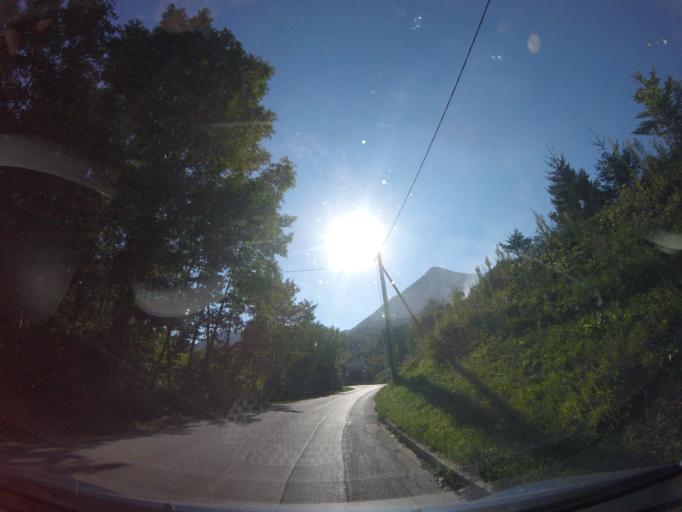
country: HR
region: Zagrebacka
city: Rude
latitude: 45.7623
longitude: 15.6648
